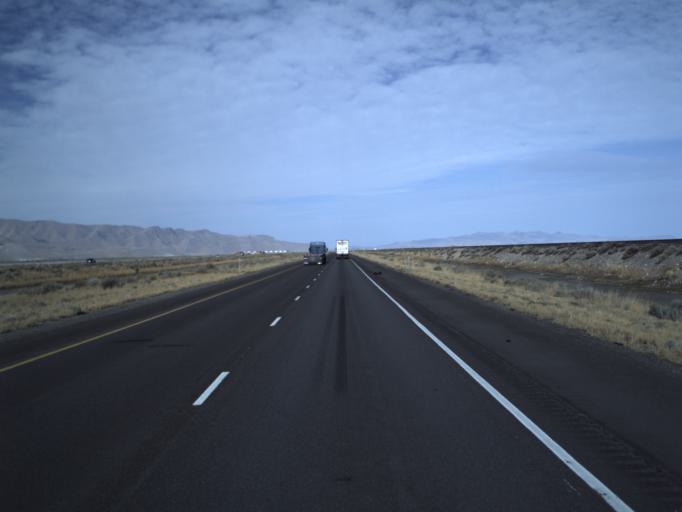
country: US
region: Utah
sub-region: Tooele County
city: Grantsville
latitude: 40.6763
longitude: -112.4033
